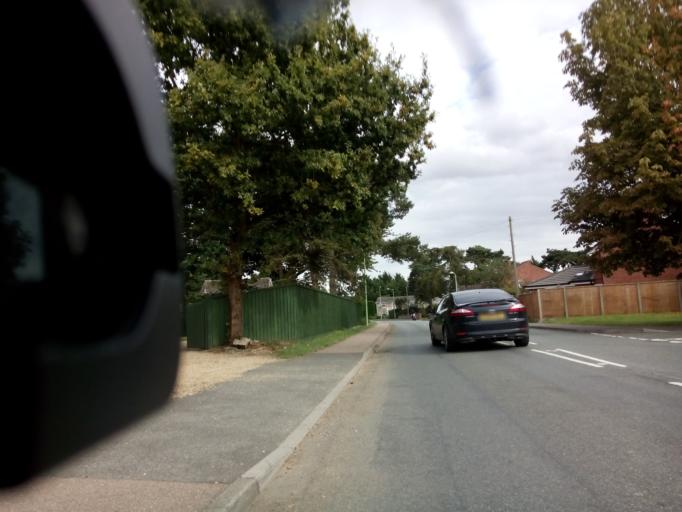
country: GB
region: England
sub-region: Suffolk
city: Capel Saint Mary
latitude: 52.0033
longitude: 1.0546
